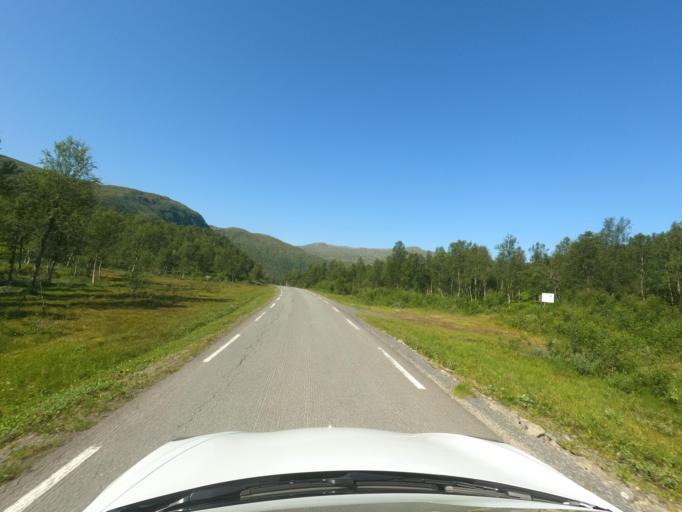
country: NO
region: Troms
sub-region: Skanland
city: Evenskjer
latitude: 68.3284
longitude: 16.5677
